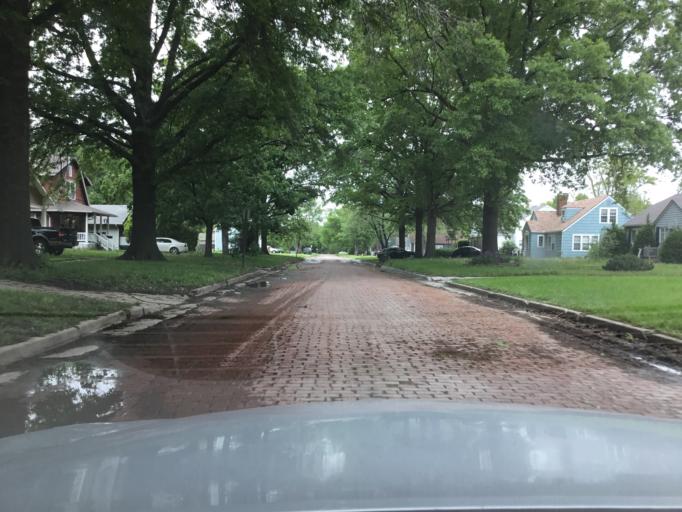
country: US
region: Kansas
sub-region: Franklin County
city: Ottawa
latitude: 38.6056
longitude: -95.2617
